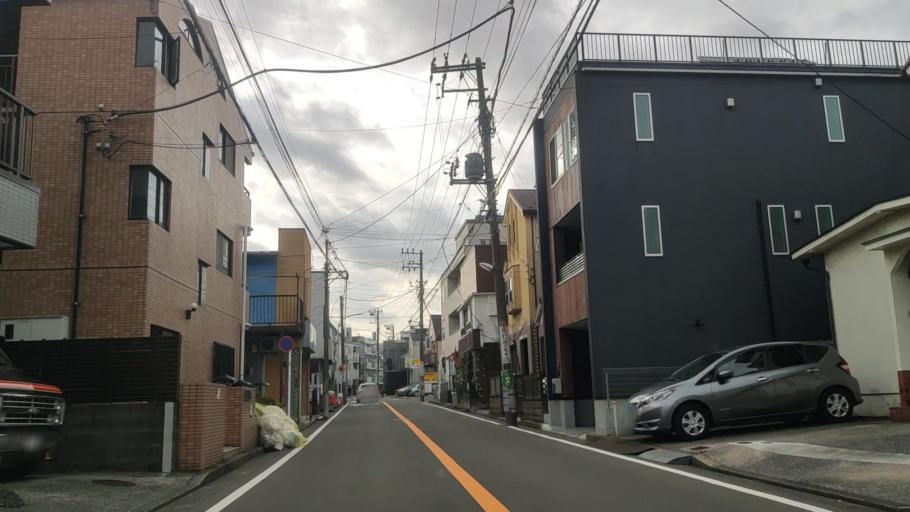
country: JP
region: Kanagawa
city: Yokohama
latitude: 35.4852
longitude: 139.6229
